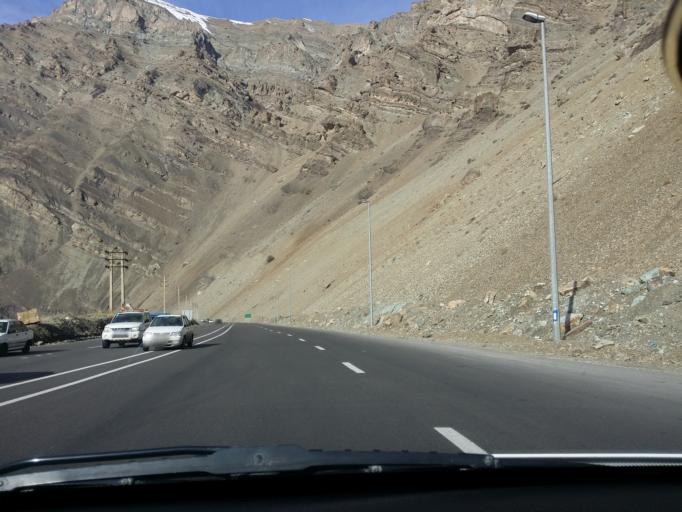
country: IR
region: Alborz
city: Karaj
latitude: 36.0118
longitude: 51.1309
